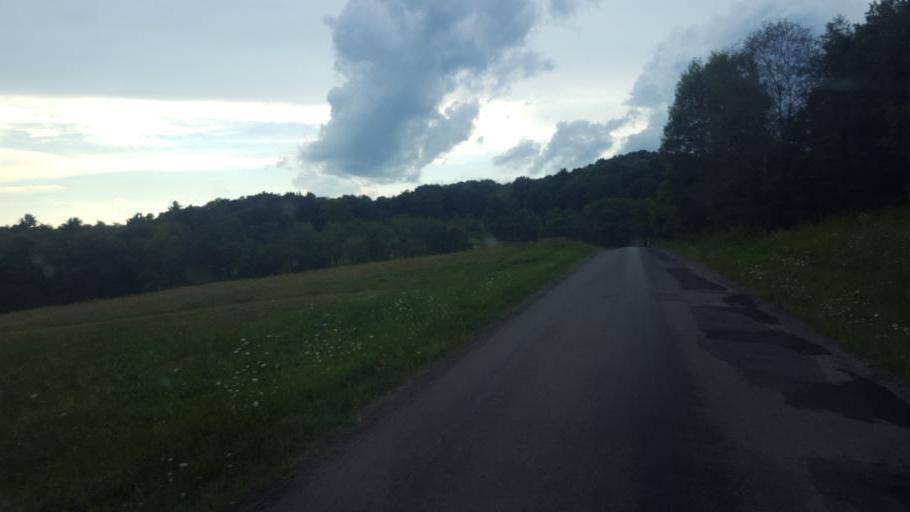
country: US
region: Pennsylvania
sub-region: Clarion County
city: Clarion
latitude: 41.1779
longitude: -79.3822
